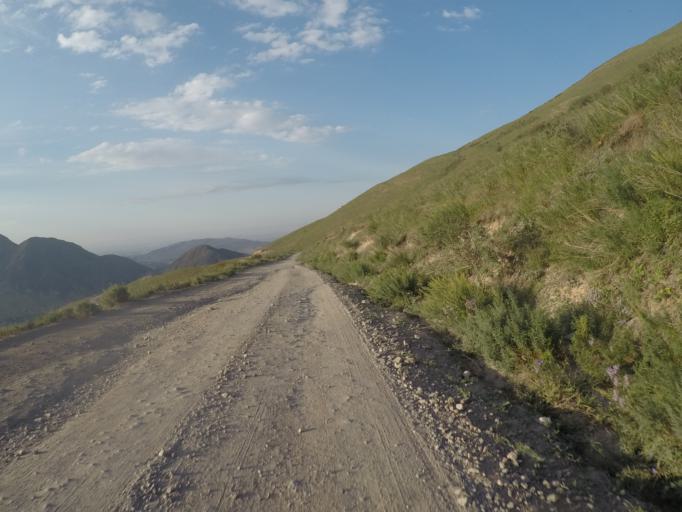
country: KG
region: Chuy
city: Bishkek
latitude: 42.6519
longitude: 74.6617
